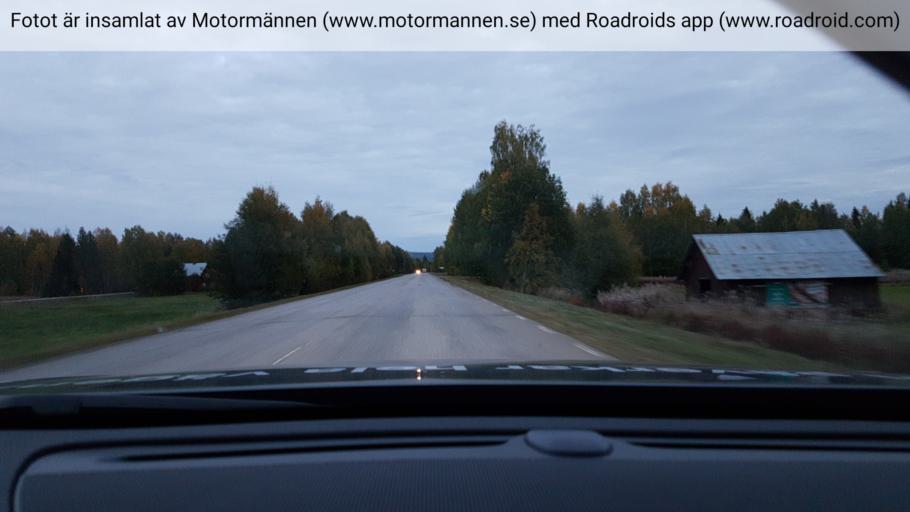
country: SE
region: Norrbotten
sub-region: Alvsbyns Kommun
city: AElvsbyn
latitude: 65.8461
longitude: 20.4756
